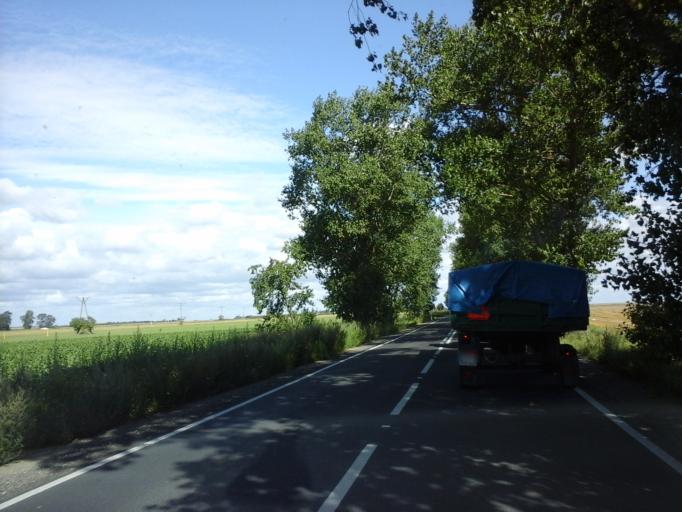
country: PL
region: West Pomeranian Voivodeship
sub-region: Powiat stargardzki
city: Stargard Szczecinski
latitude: 53.2547
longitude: 15.1007
